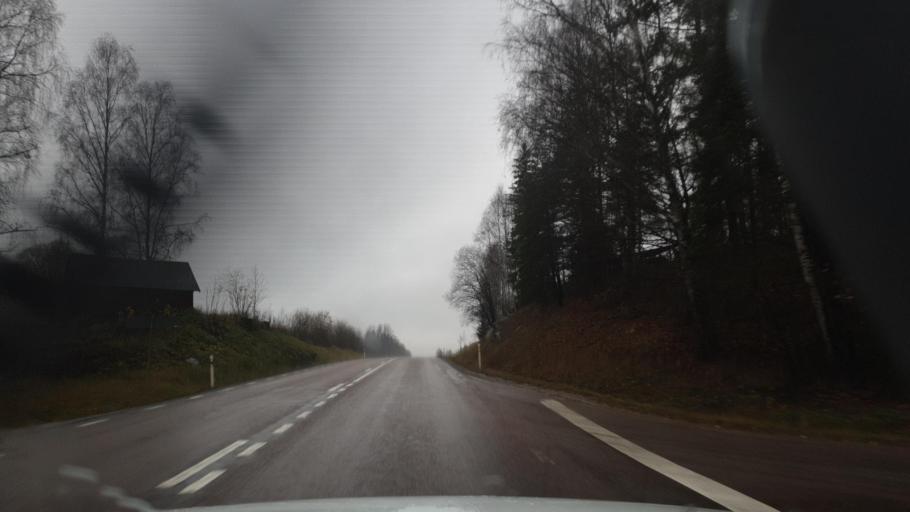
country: SE
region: Vaermland
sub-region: Arvika Kommun
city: Arvika
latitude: 59.6673
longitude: 12.8419
